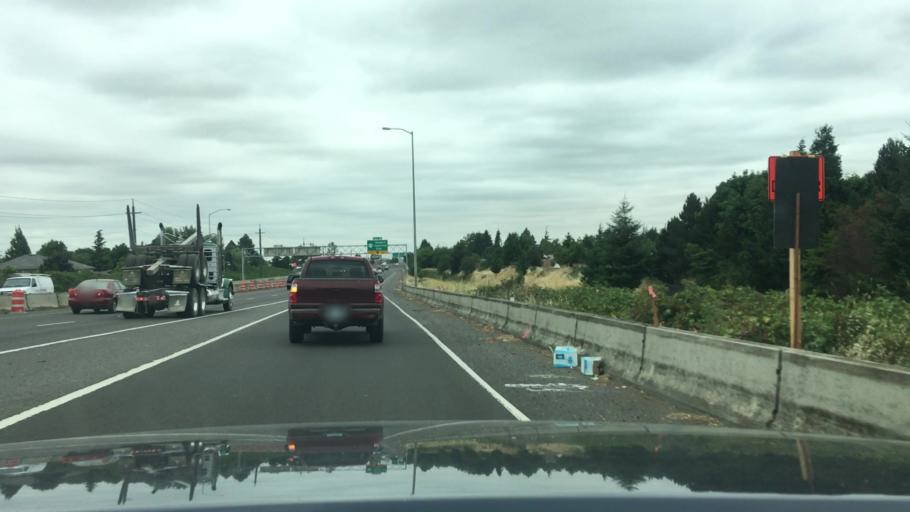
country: US
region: Oregon
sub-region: Lane County
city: Eugene
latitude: 44.0873
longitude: -123.1714
